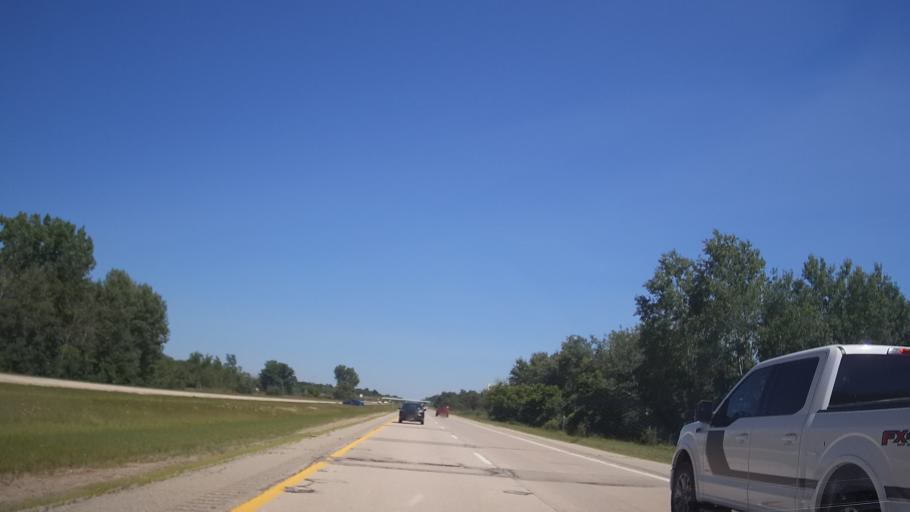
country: US
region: Michigan
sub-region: Clare County
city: Clare
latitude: 43.8038
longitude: -84.6787
